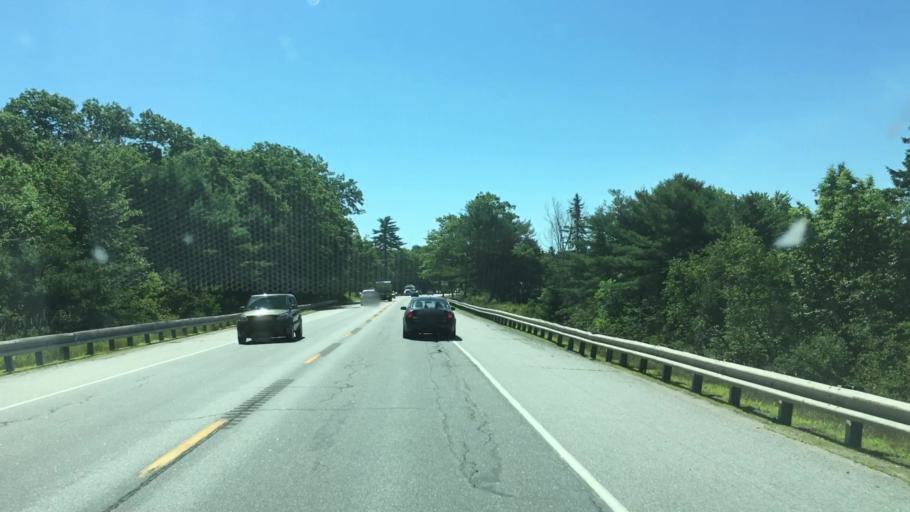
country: US
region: Maine
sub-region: Hancock County
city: Orland
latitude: 44.5677
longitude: -68.7206
